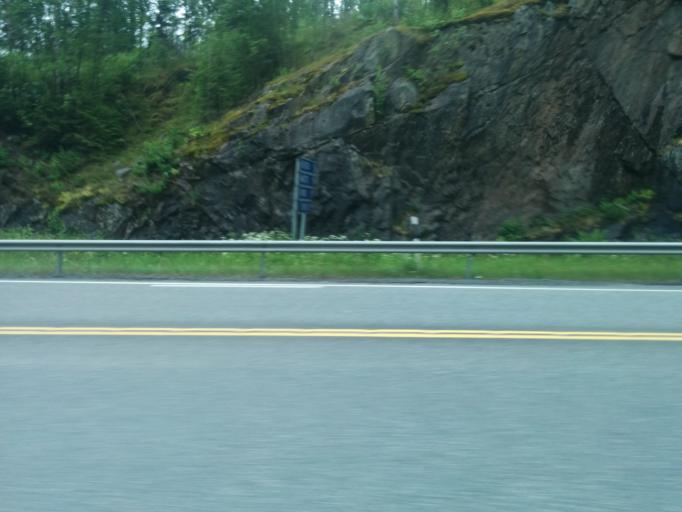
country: FI
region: Pirkanmaa
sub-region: Tampere
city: Orivesi
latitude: 61.6849
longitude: 24.3520
